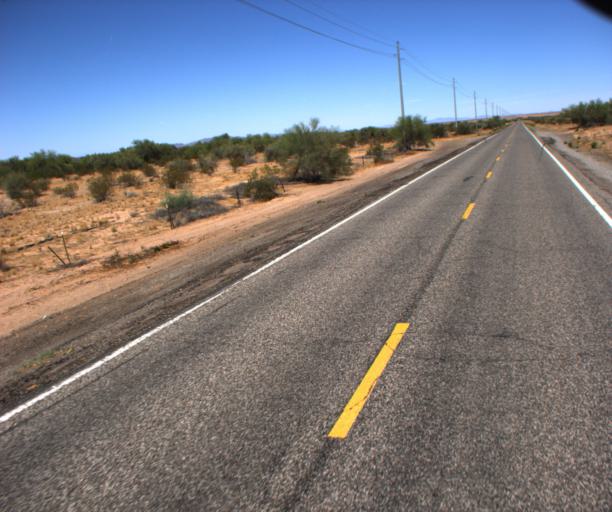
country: US
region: Arizona
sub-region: La Paz County
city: Cienega Springs
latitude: 33.9797
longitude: -114.0571
